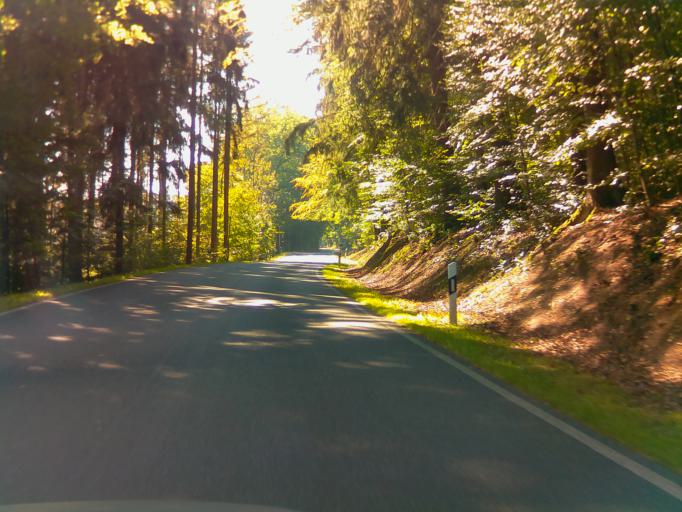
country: DE
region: Thuringia
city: Wurzbach
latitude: 50.4803
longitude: 11.4701
